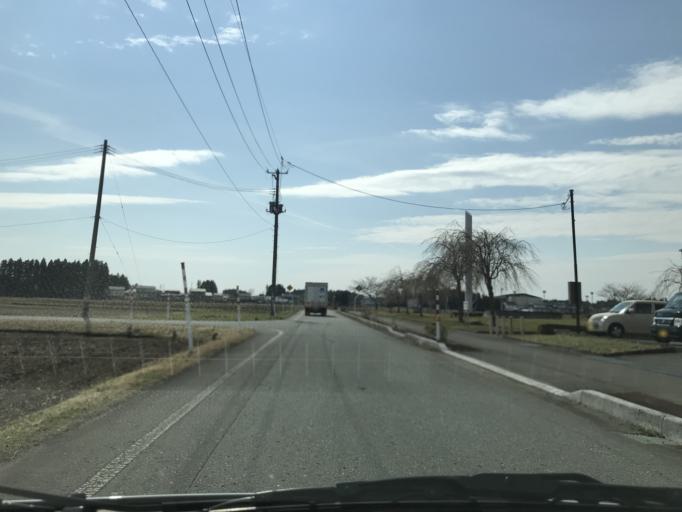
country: JP
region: Iwate
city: Mizusawa
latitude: 39.1288
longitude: 141.0704
